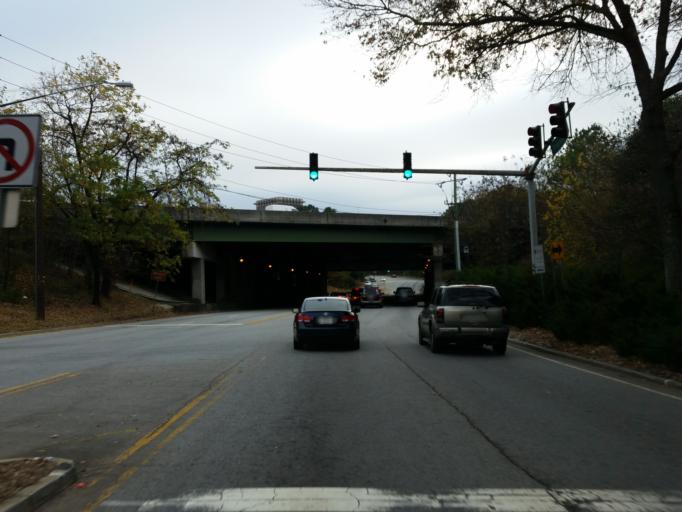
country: US
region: Georgia
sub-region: Fulton County
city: Sandy Springs
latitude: 33.9147
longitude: -84.3516
